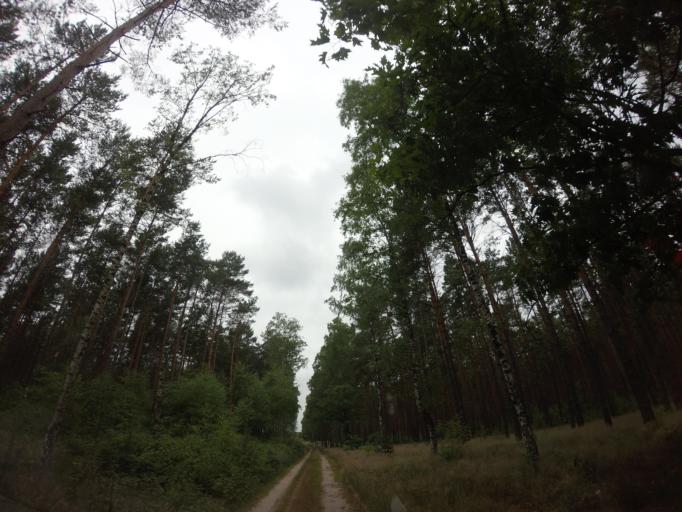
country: PL
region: West Pomeranian Voivodeship
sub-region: Powiat choszczenski
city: Drawno
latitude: 53.1488
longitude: 15.7020
